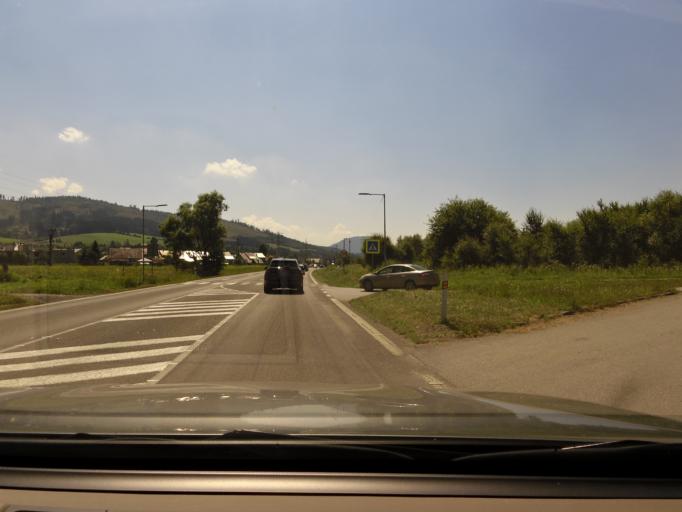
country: SK
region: Zilinsky
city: Kysucke Nove Mesto
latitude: 49.3440
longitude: 18.8100
